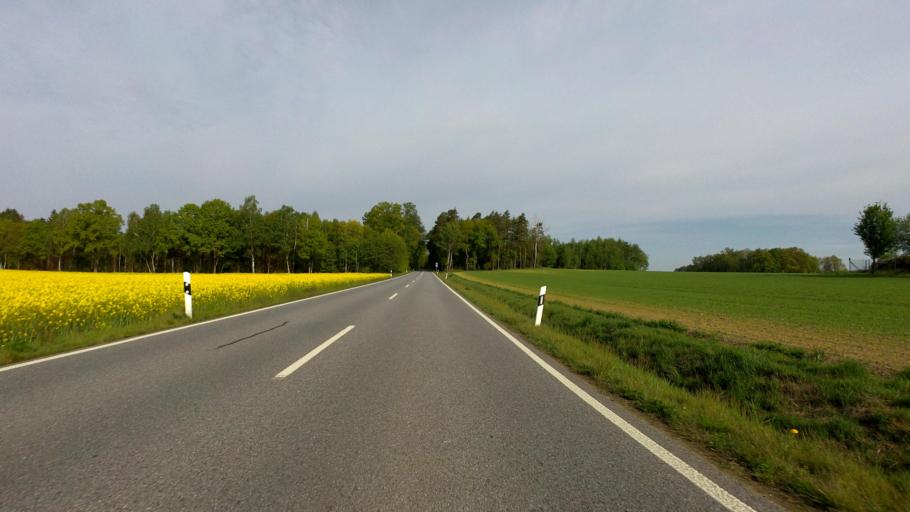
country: DE
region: Saxony
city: Stolpen
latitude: 51.0694
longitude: 14.0461
